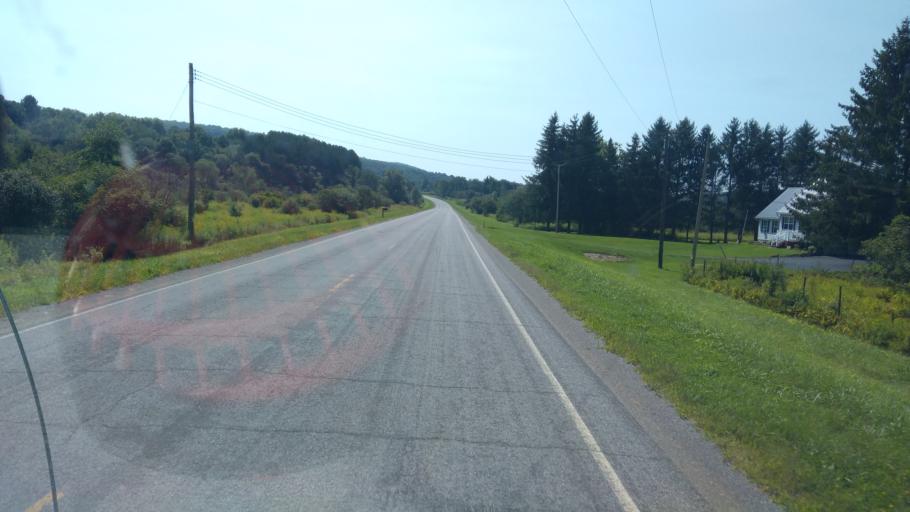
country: US
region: New York
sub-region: Allegany County
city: Belmont
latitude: 42.3384
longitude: -77.9304
